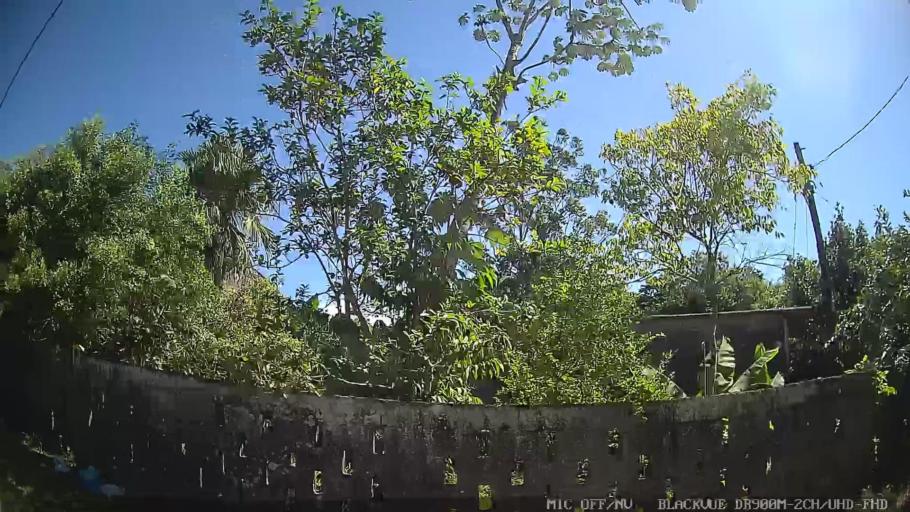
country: BR
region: Sao Paulo
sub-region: Iguape
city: Iguape
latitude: -24.6932
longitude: -47.5659
